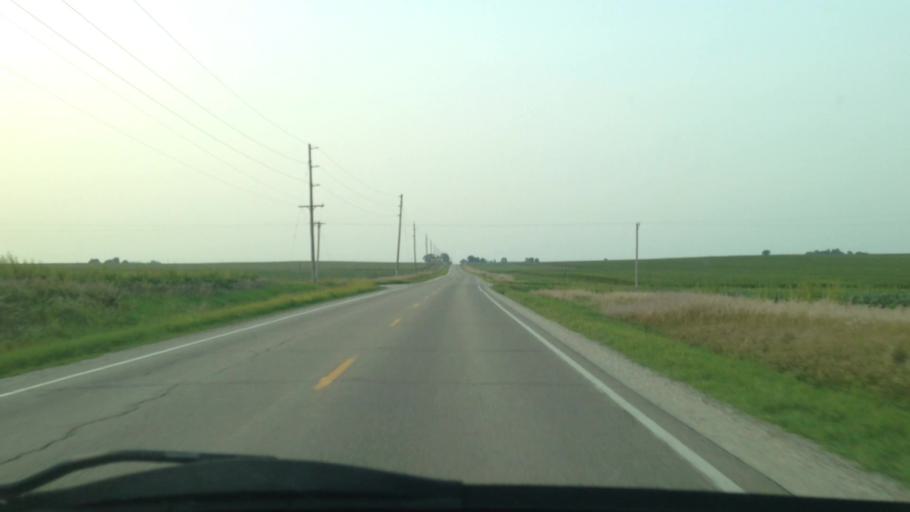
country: US
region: Iowa
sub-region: Iowa County
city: Marengo
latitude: 41.9483
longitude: -92.0852
